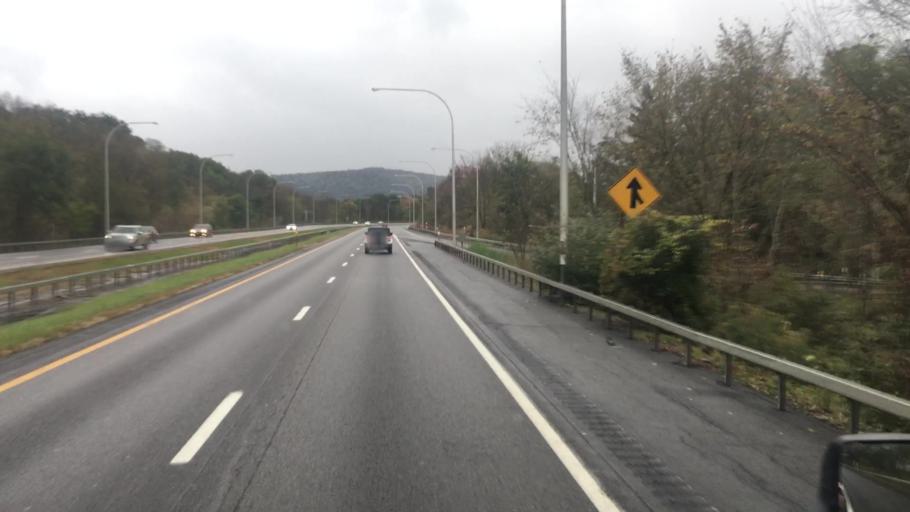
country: US
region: New York
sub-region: Broome County
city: Endicott
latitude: 42.0960
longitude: -76.0323
